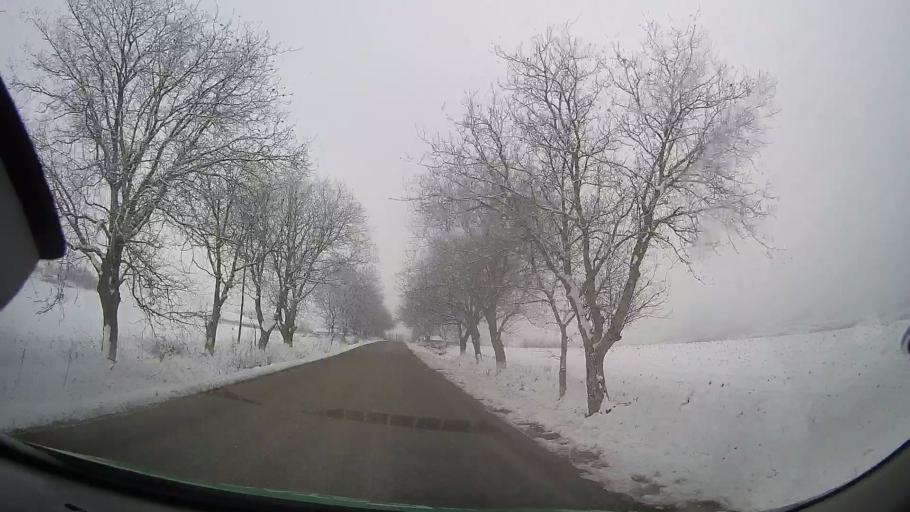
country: RO
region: Bacau
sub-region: Comuna Oncesti
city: Oncesti
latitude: 46.4465
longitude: 27.2643
